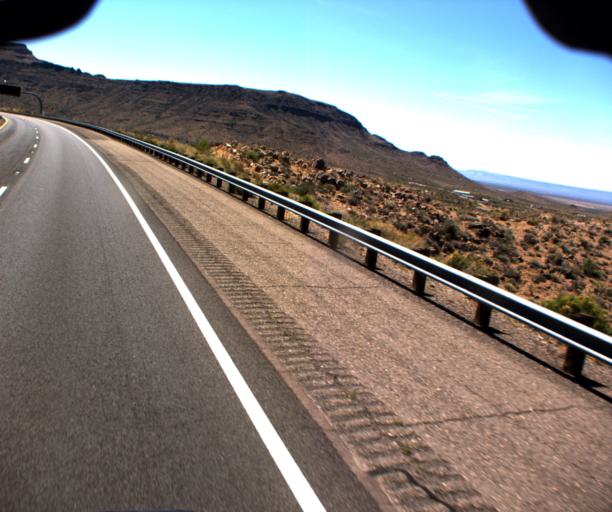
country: US
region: Arizona
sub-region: Mohave County
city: Golden Valley
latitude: 35.2298
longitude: -114.1361
